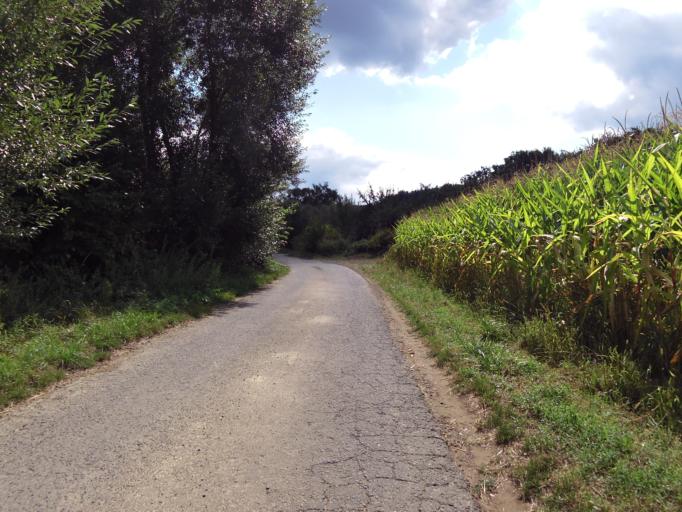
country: DE
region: Hesse
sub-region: Regierungsbezirk Darmstadt
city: Brensbach
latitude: 49.7706
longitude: 8.8917
